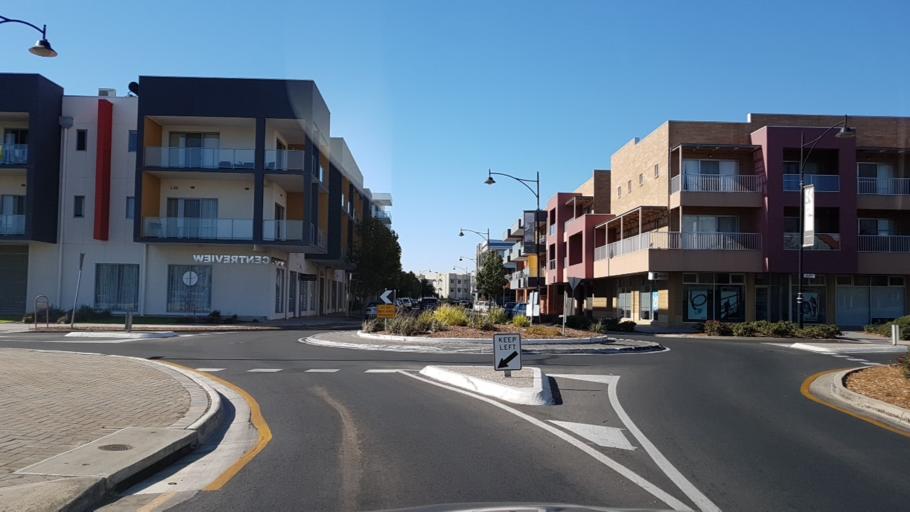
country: AU
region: South Australia
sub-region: Salisbury
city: Ingle Farm
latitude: -34.8083
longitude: 138.6148
